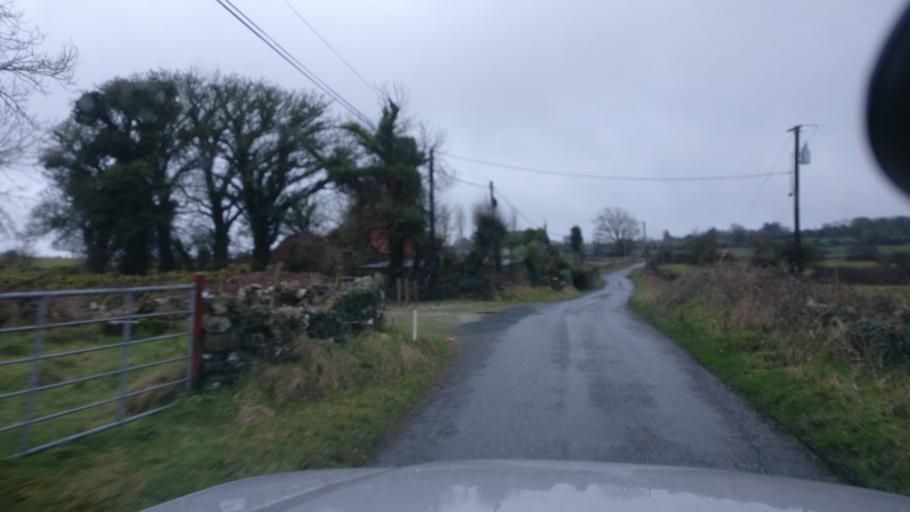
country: IE
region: Connaught
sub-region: County Galway
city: Loughrea
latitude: 53.1764
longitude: -8.6507
